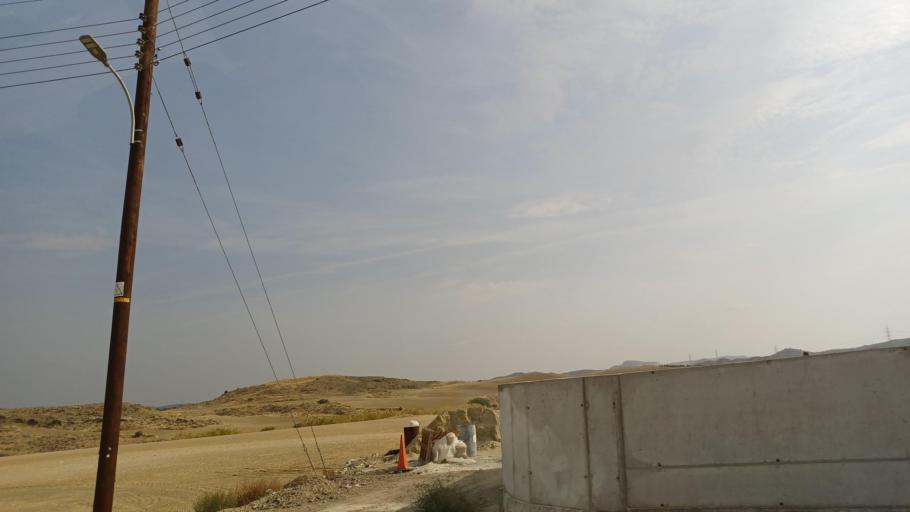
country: CY
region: Larnaka
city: Troulloi
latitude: 35.0005
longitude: 33.5748
